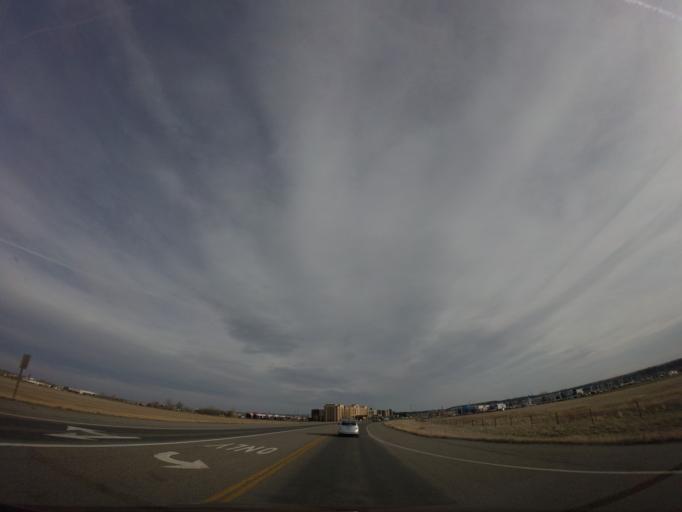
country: US
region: Montana
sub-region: Yellowstone County
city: Billings
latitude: 45.7360
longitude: -108.6125
